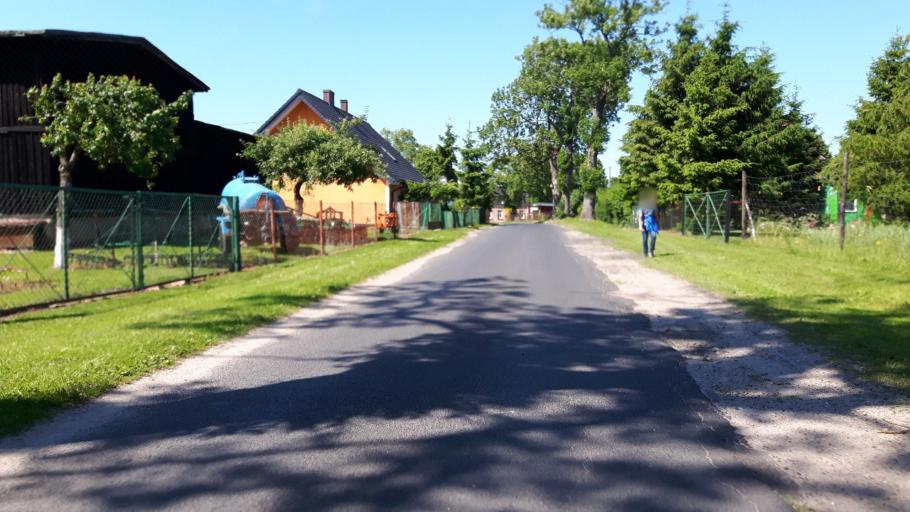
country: PL
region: Pomeranian Voivodeship
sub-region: Powiat slupski
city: Glowczyce
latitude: 54.6767
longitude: 17.4238
